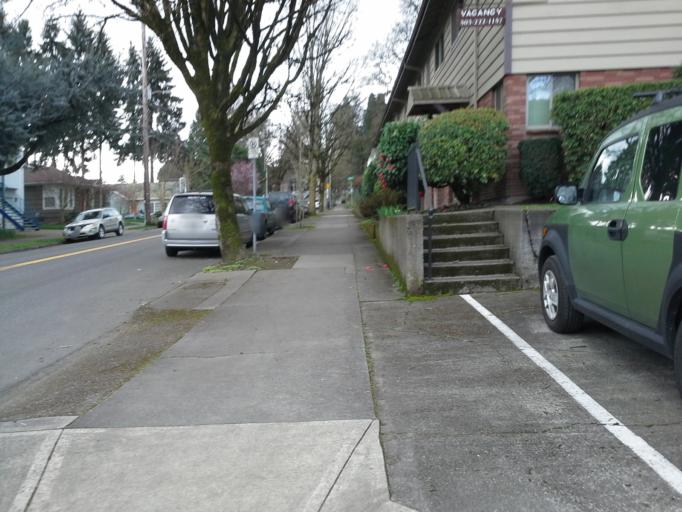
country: US
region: Oregon
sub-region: Multnomah County
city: Portland
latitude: 45.4965
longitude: -122.6761
